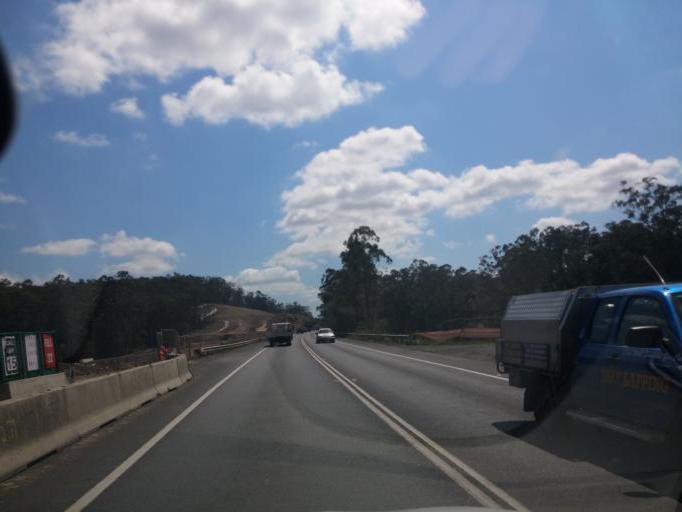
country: AU
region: New South Wales
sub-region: Port Macquarie-Hastings
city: North Shore
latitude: -31.2723
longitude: 152.8124
